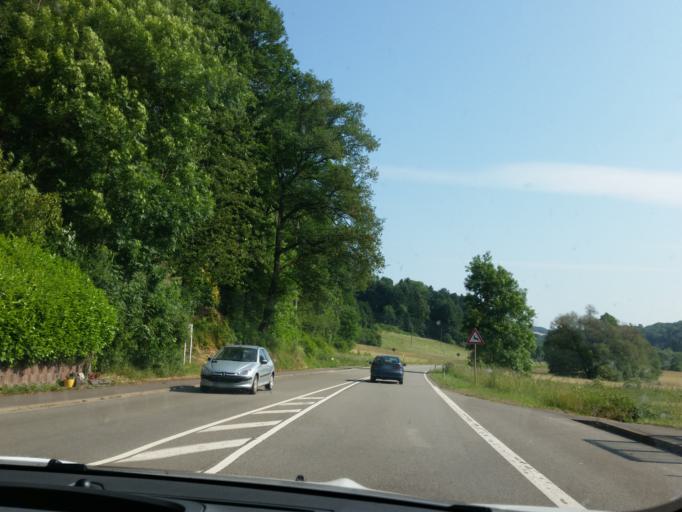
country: DE
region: Saarland
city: Schmelz
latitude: 49.4556
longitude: 6.8482
